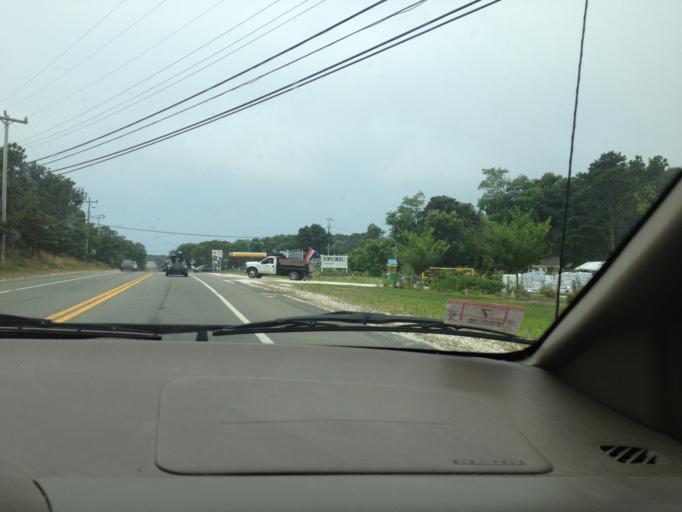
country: US
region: Massachusetts
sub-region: Barnstable County
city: Wellfleet
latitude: 41.9170
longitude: -69.9928
